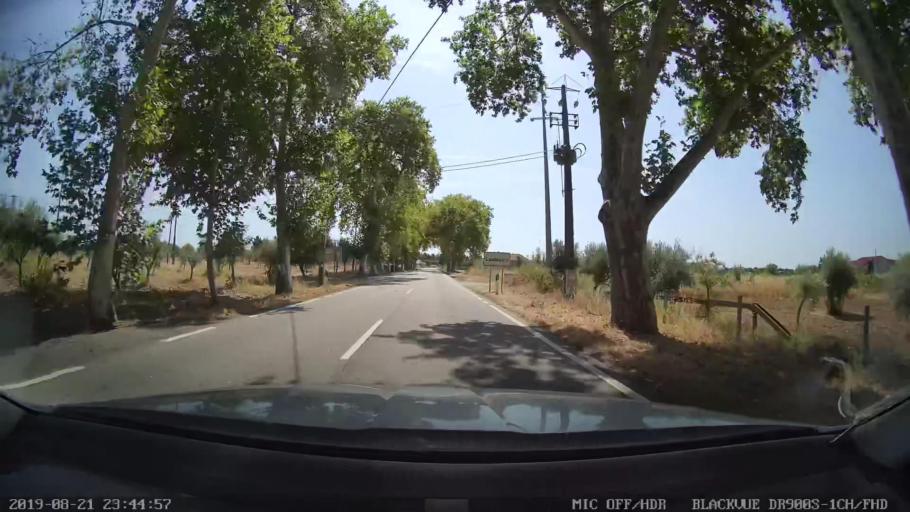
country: PT
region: Castelo Branco
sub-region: Idanha-A-Nova
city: Idanha-a-Nova
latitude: 39.8430
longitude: -7.2708
